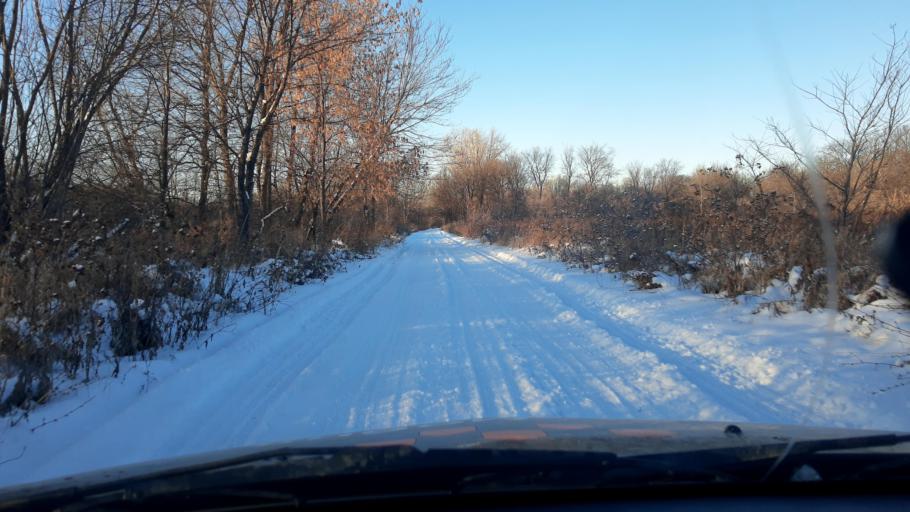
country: RU
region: Bashkortostan
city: Ufa
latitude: 54.6582
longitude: 55.9696
